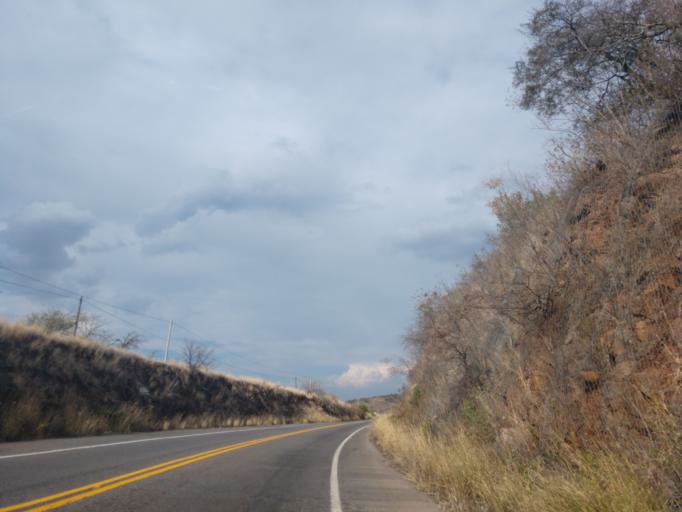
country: MX
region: Jalisco
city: La Manzanilla de la Paz
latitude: 20.0788
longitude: -103.1697
